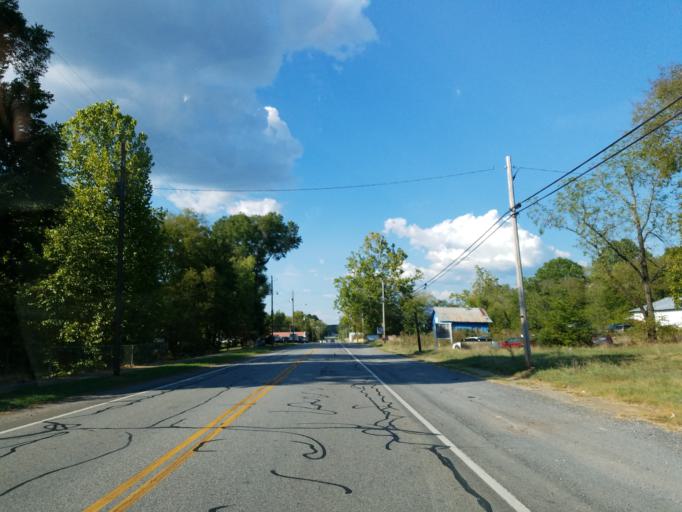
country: US
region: Georgia
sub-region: Bartow County
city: Rydal
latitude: 34.4987
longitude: -84.7096
